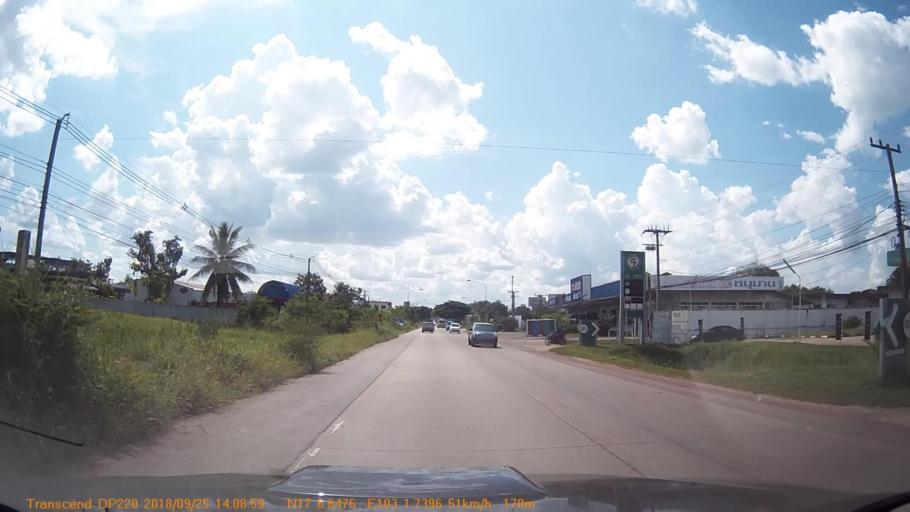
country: TH
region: Changwat Udon Thani
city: Kumphawapi
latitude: 17.1108
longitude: 103.0289
